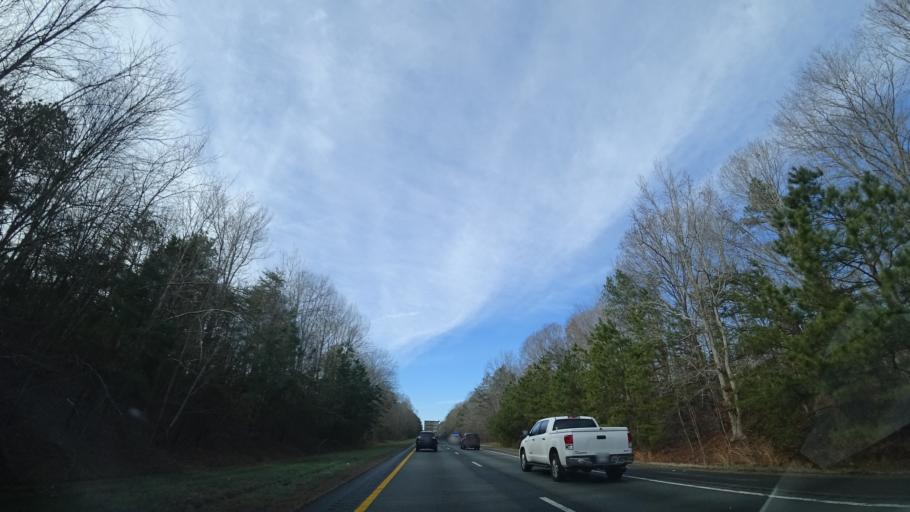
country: US
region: Virginia
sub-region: New Kent County
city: New Kent
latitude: 37.4911
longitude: -77.0015
